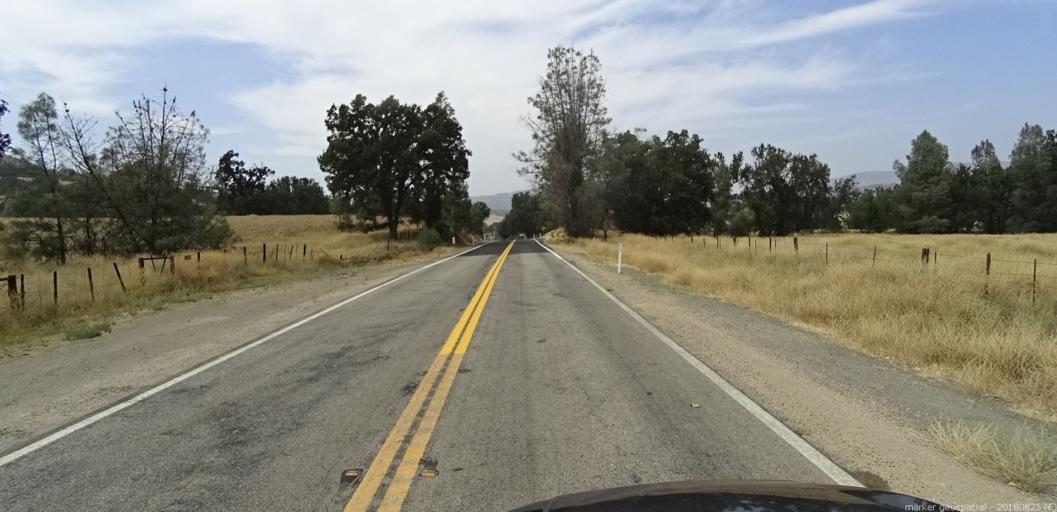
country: US
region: California
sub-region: Fresno County
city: Coalinga
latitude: 36.1899
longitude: -120.7065
